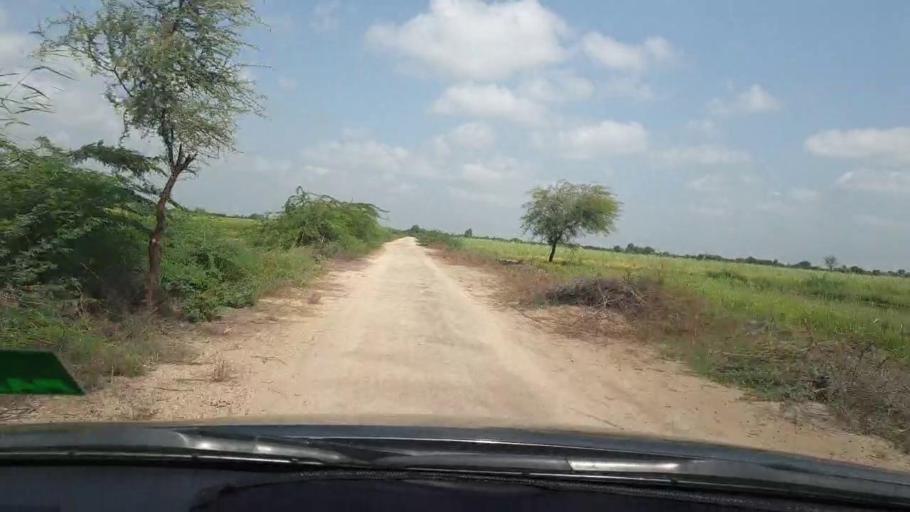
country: PK
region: Sindh
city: Tando Bago
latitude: 24.8686
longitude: 69.0355
